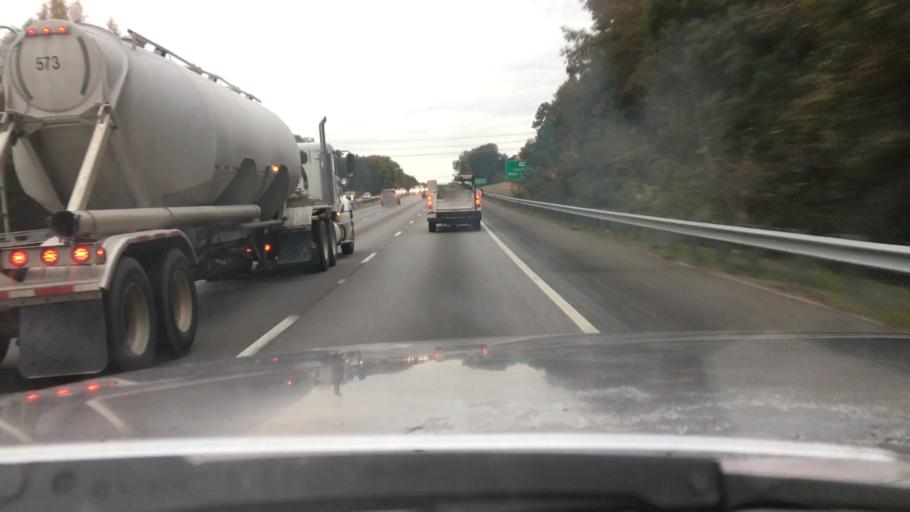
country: US
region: South Carolina
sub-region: Lexington County
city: Saint Andrews
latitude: 34.0233
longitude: -81.1314
